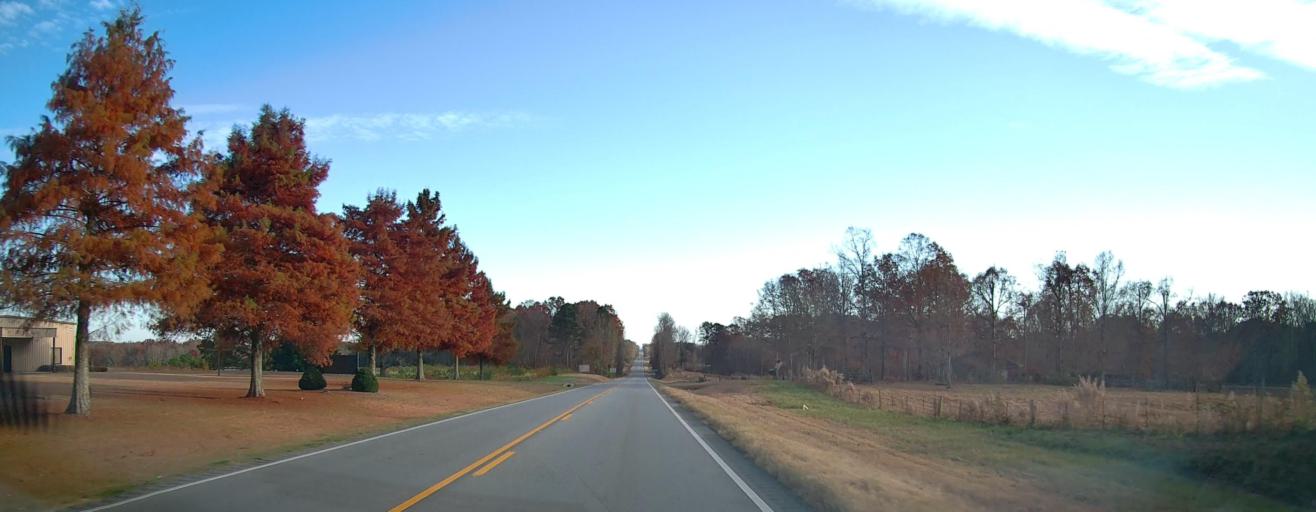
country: US
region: Alabama
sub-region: Marshall County
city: Arab
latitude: 34.2832
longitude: -86.5852
